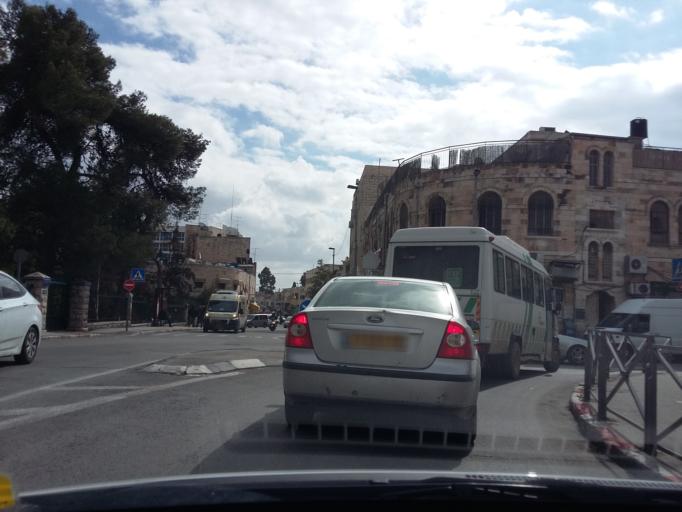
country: PS
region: West Bank
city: East Jerusalem
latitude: 31.7866
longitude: 35.2307
